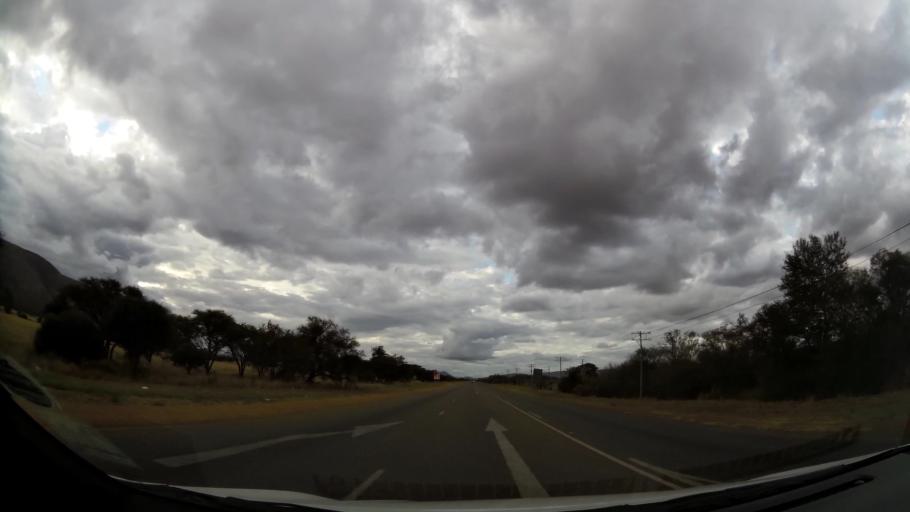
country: ZA
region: Limpopo
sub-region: Waterberg District Municipality
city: Mokopane
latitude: -24.2661
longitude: 28.9833
